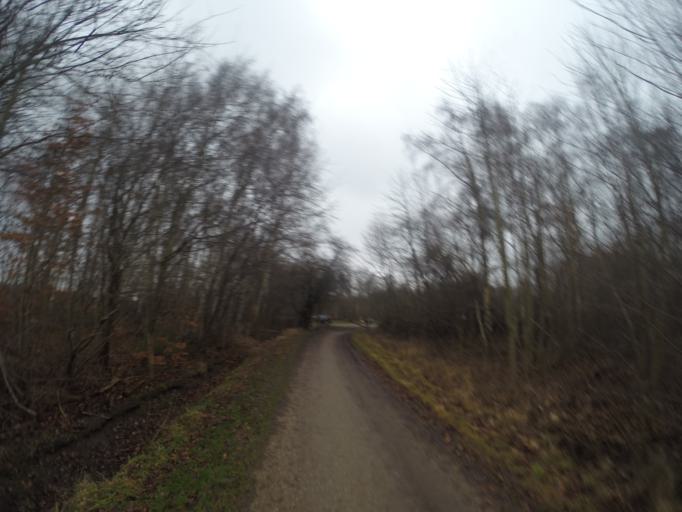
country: DK
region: Capital Region
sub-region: Hoje-Taastrup Kommune
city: Taastrup
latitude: 55.6902
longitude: 12.3220
